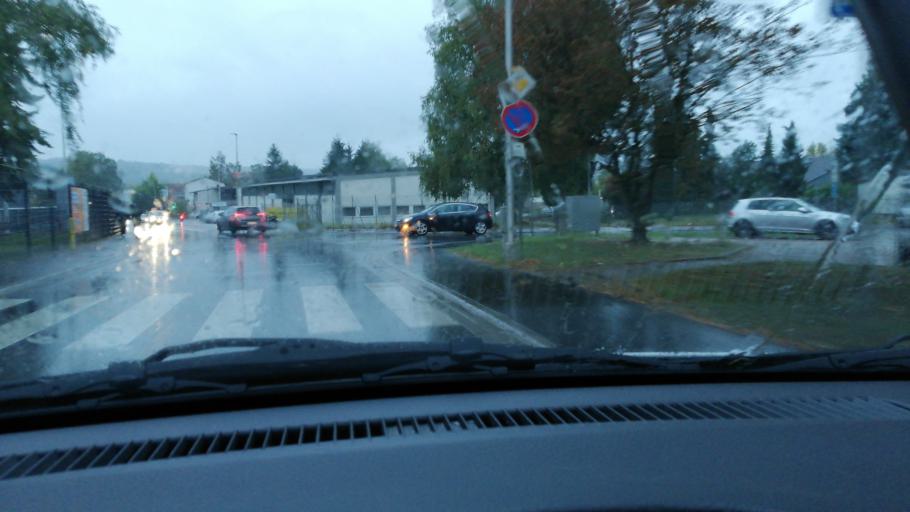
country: DE
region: Bavaria
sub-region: Regierungsbezirk Unterfranken
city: Marktheidenfeld
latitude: 49.8483
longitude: 9.6166
